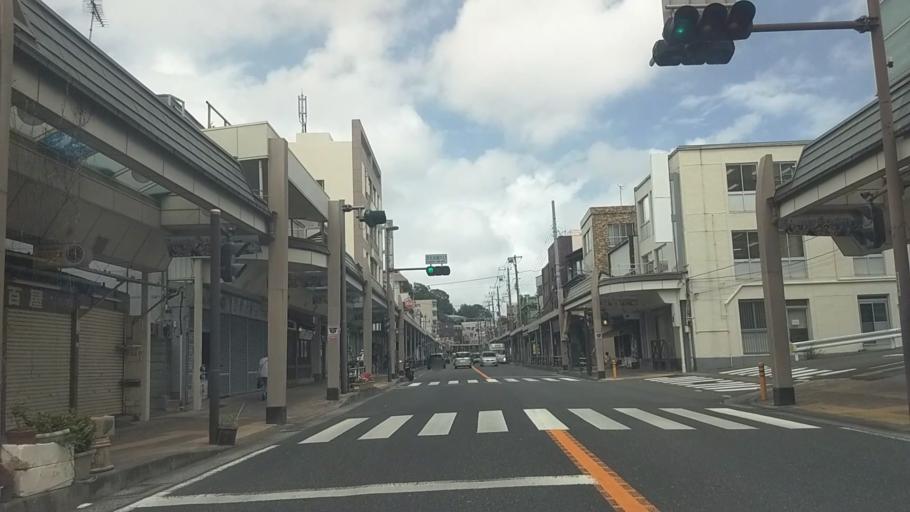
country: JP
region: Kanagawa
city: Yokosuka
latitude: 35.2734
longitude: 139.6703
